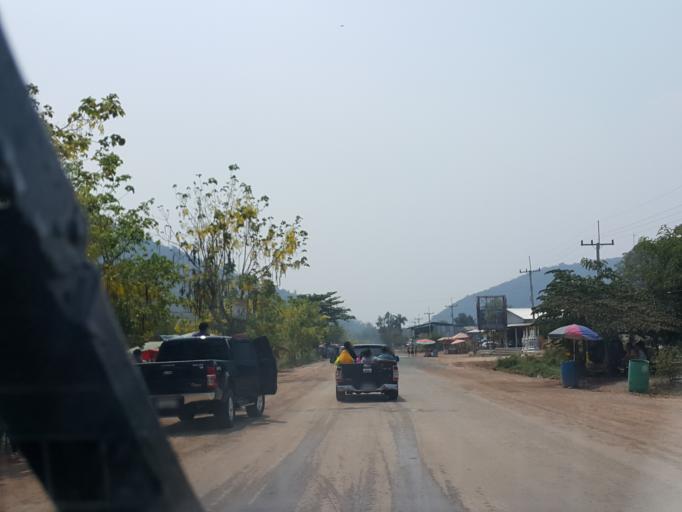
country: TH
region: Nakhon Sawan
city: Mae Wong
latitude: 15.8983
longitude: 99.4699
